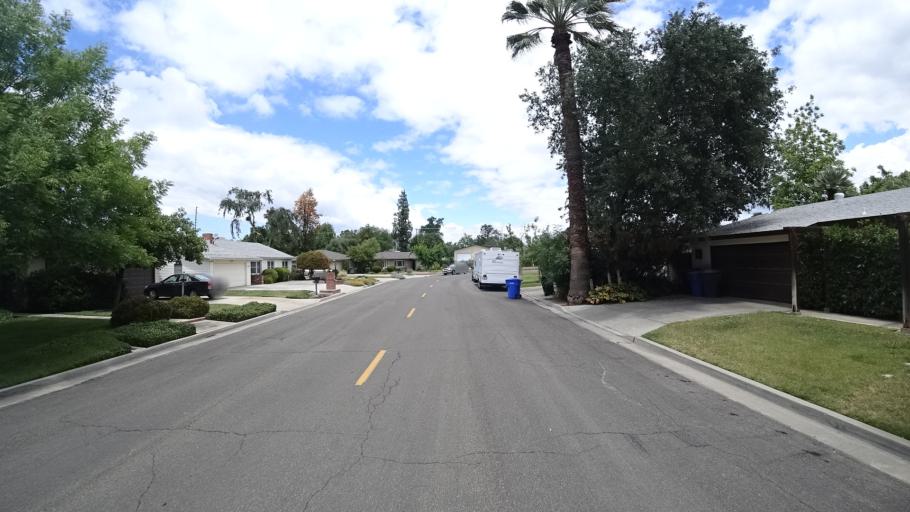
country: US
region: California
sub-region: Kings County
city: Hanford
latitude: 36.3490
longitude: -119.6541
